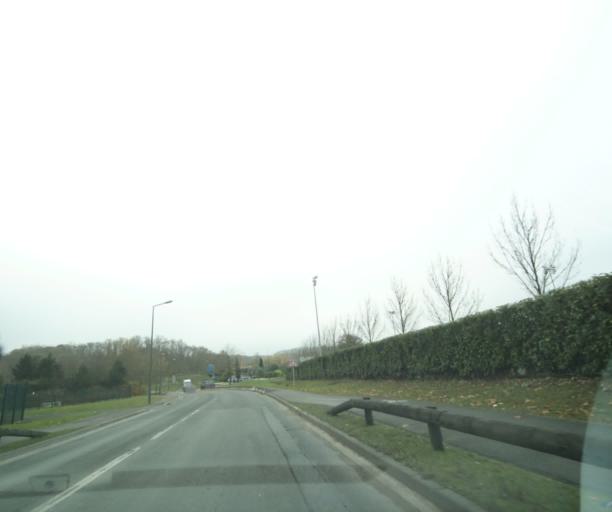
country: FR
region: Ile-de-France
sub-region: Departement de Seine-et-Marne
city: Villeparisis
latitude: 48.9362
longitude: 2.6017
